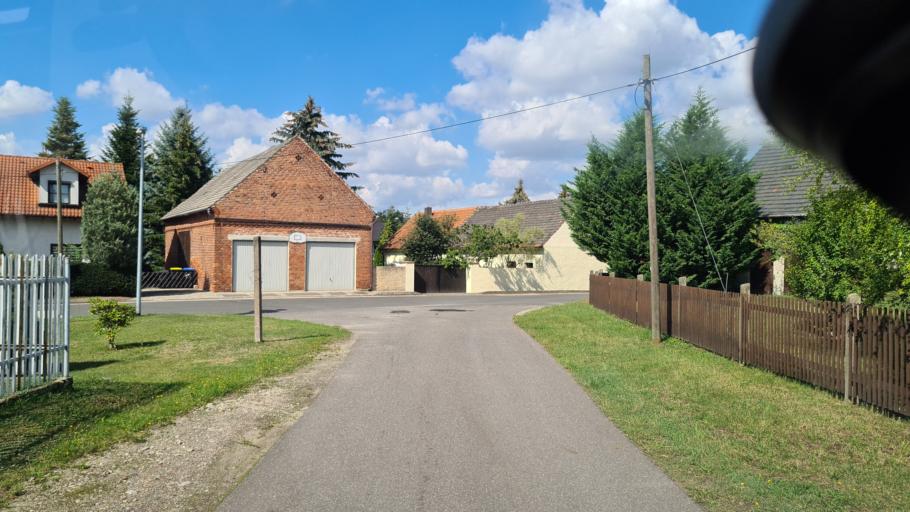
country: DE
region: Brandenburg
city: Spremberg
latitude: 51.6494
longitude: 14.3330
